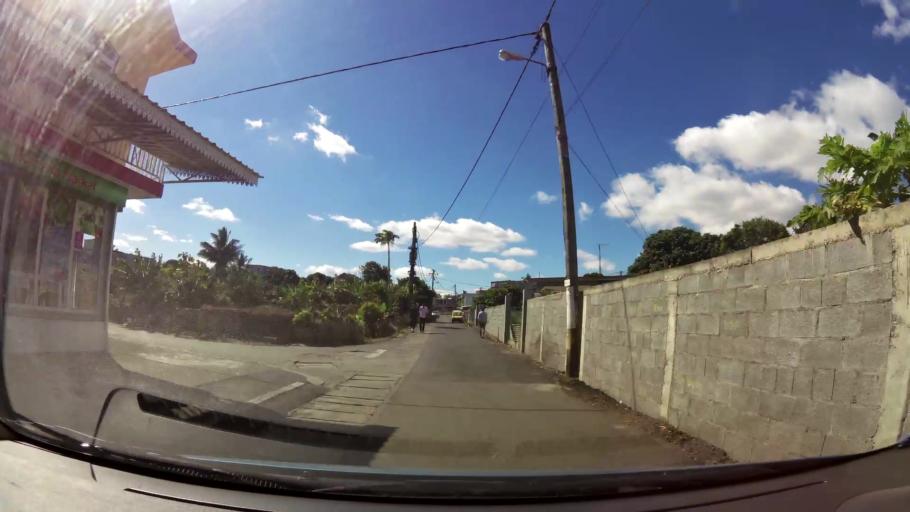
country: MU
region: Plaines Wilhems
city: Vacoas
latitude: -20.2939
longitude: 57.4794
